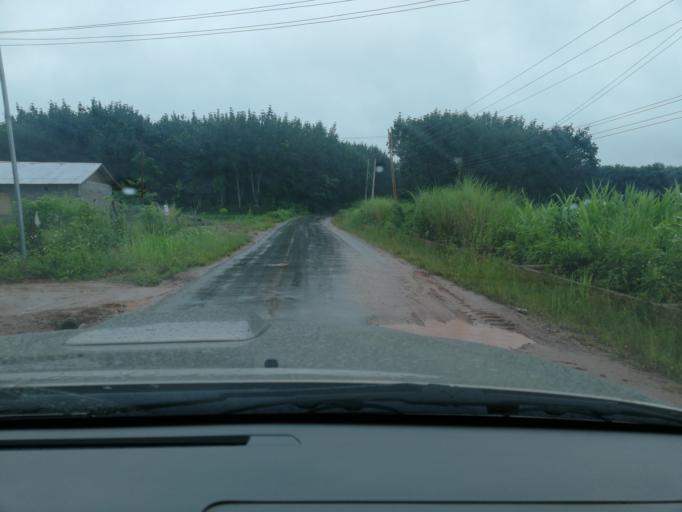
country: LA
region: Loungnamtha
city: Louang Namtha
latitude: 20.9774
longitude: 101.3847
